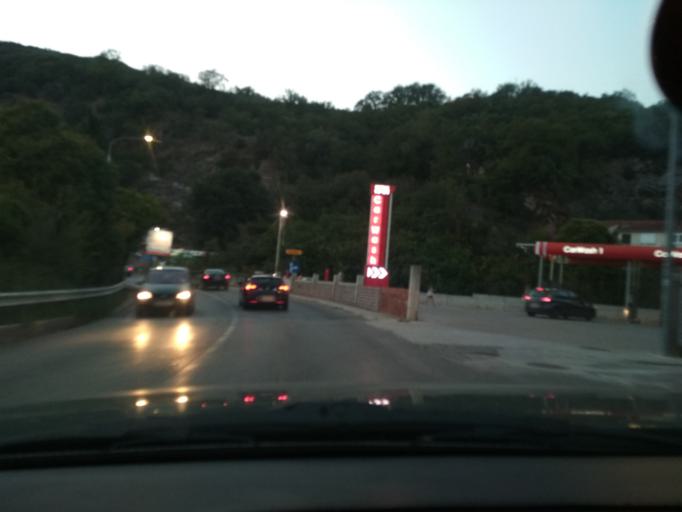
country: ME
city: Igalo
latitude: 42.4615
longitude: 18.5206
